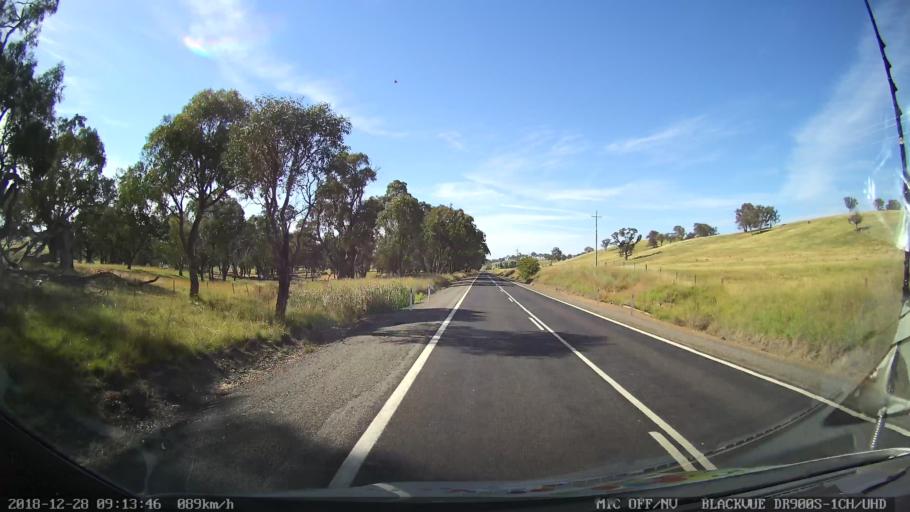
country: AU
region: New South Wales
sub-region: Upper Lachlan Shire
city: Crookwell
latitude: -34.2731
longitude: 149.3446
